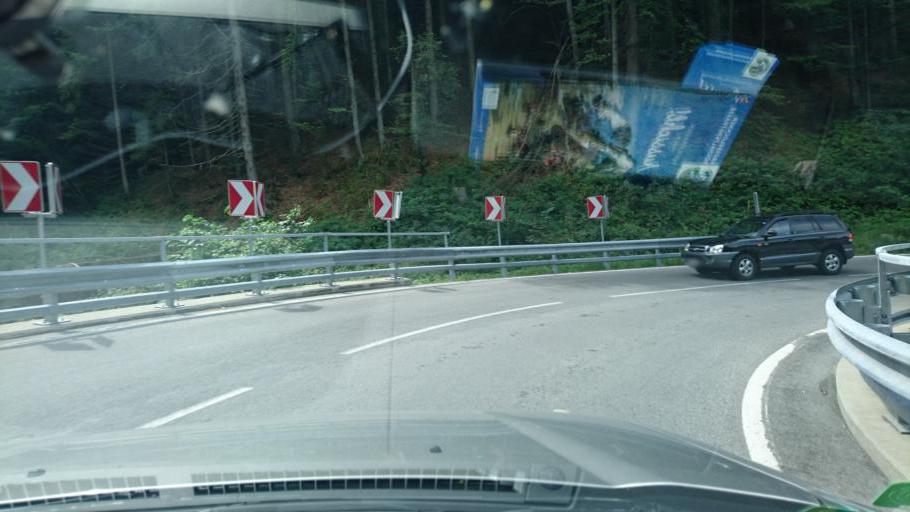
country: AT
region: Carinthia
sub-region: Politischer Bezirk Villach Land
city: Arnoldstein
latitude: 46.5267
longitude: 13.7520
